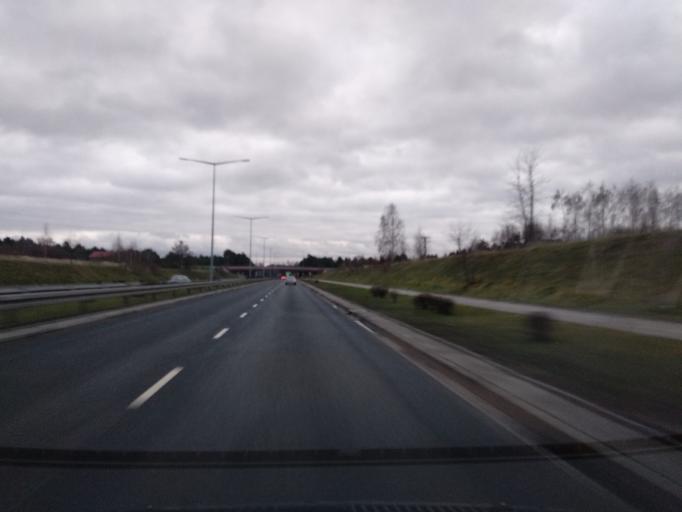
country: PL
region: Greater Poland Voivodeship
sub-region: Powiat koninski
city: Stare Miasto
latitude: 52.1952
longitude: 18.2254
